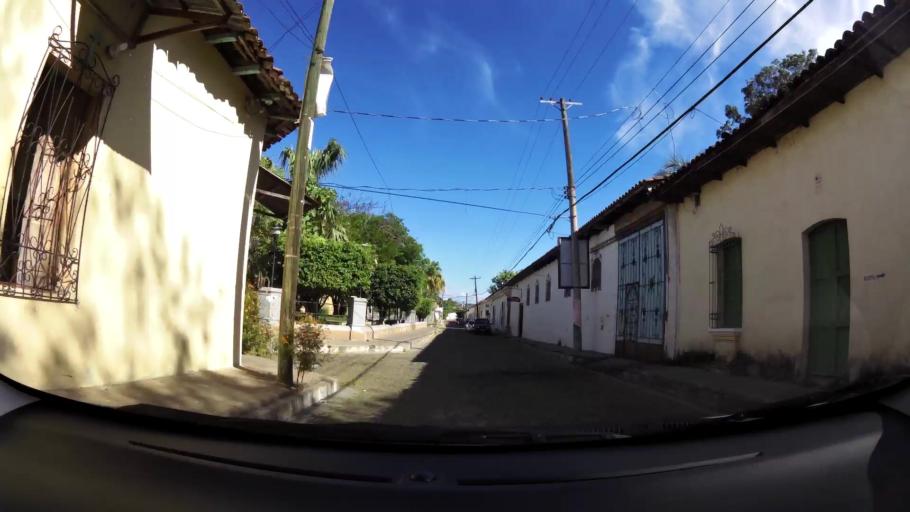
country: SV
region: Cuscatlan
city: Suchitoto
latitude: 13.9386
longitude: -89.0278
